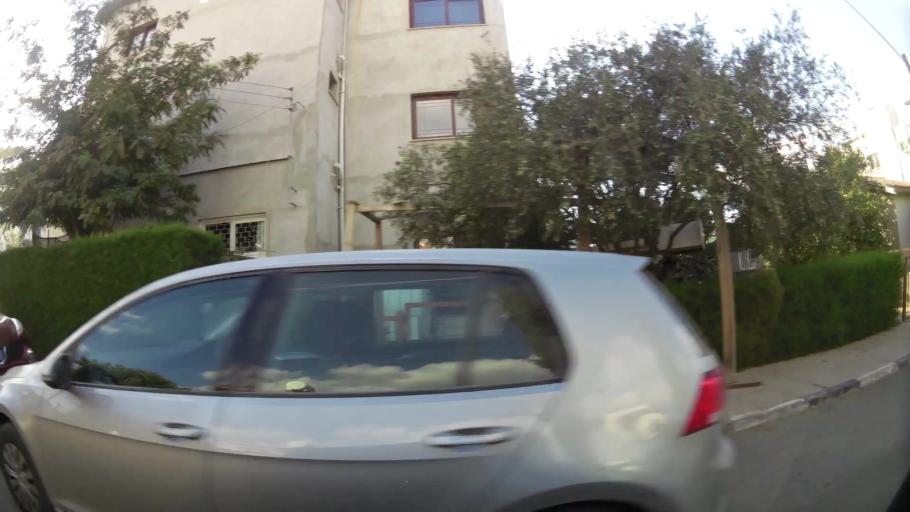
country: CY
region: Lefkosia
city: Nicosia
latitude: 35.2004
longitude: 33.3617
